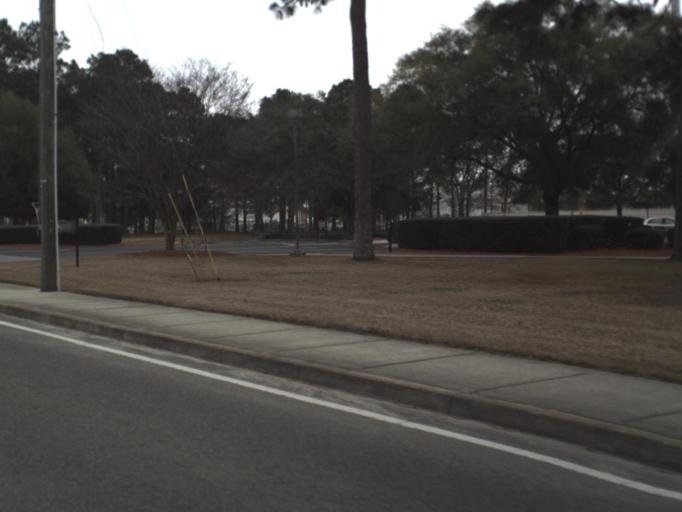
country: US
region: Florida
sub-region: Bay County
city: Cedar Grove
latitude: 30.1749
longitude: -85.6403
